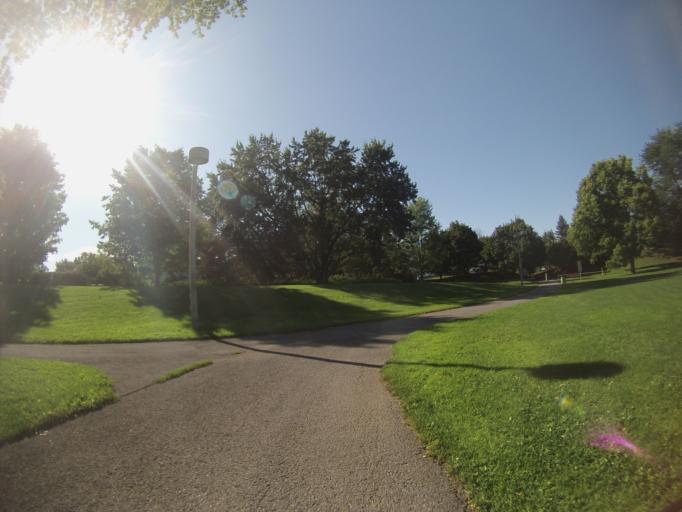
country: CA
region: Ontario
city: Bells Corners
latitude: 45.3476
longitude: -75.7535
